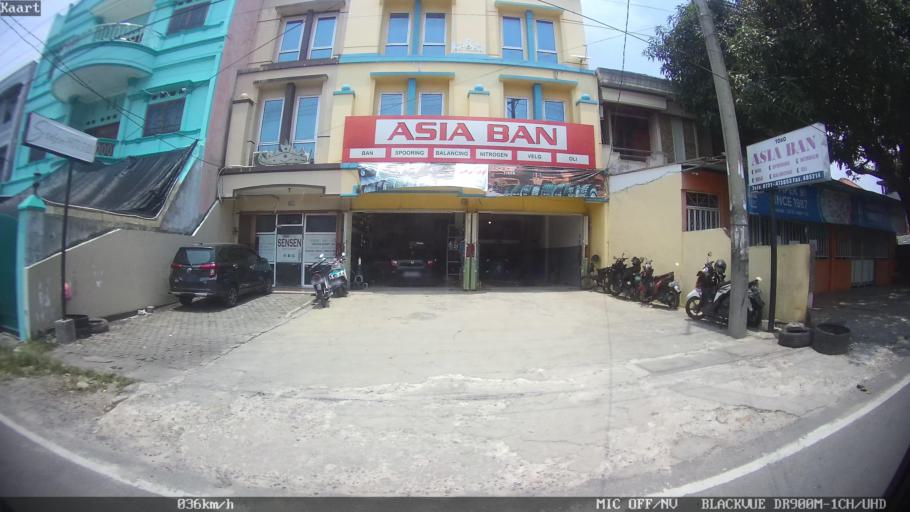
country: ID
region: Lampung
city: Bandarlampung
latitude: -5.4397
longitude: 105.2678
